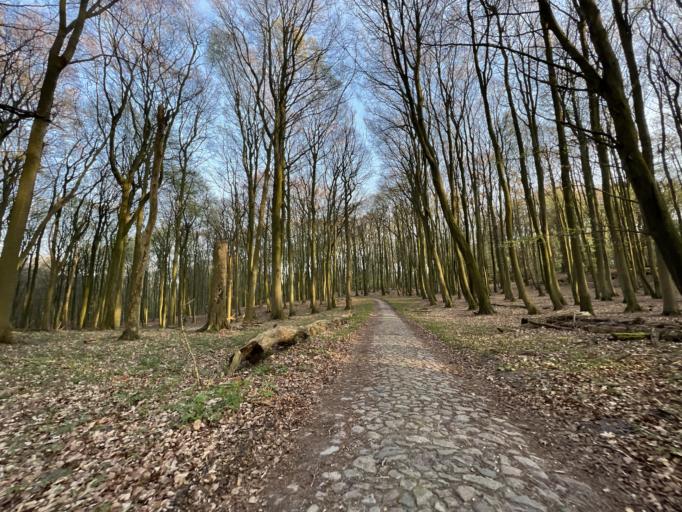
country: DE
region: Mecklenburg-Vorpommern
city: Sassnitz
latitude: 54.5321
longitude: 13.6527
